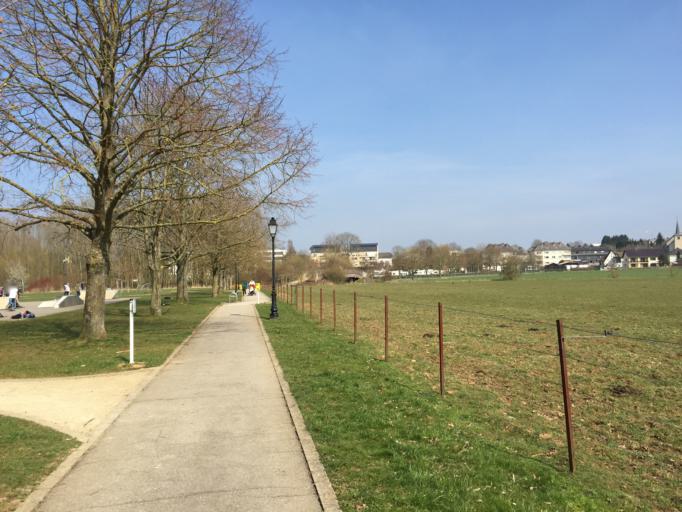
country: LU
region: Luxembourg
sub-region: Canton de Luxembourg
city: Hesperange
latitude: 49.5690
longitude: 6.1557
